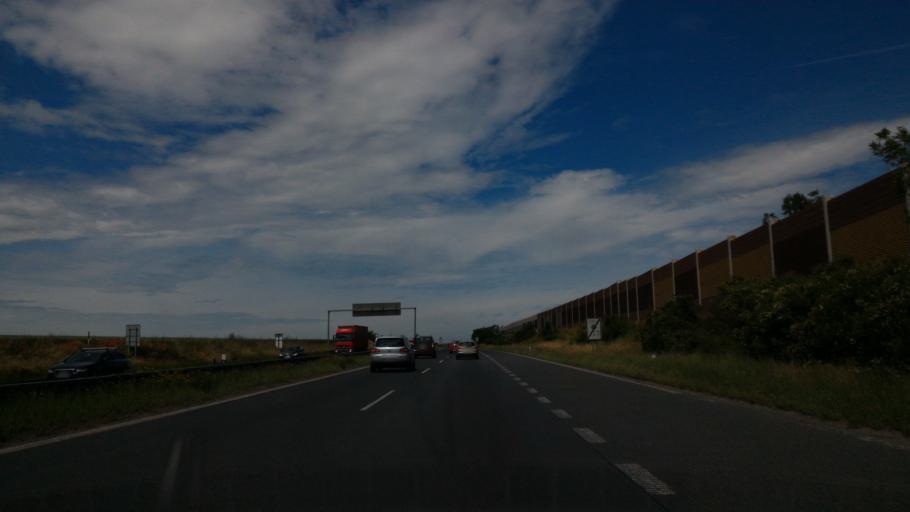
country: CZ
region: Central Bohemia
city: Zdiby
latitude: 50.1606
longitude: 14.4792
